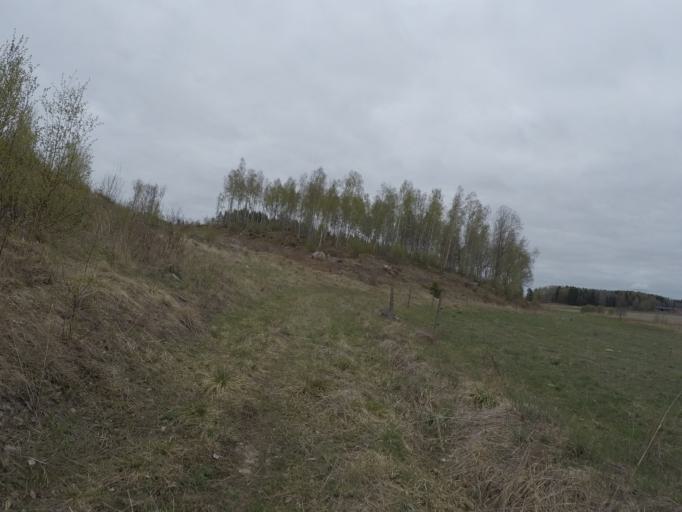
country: SE
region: Soedermanland
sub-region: Eskilstuna Kommun
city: Kvicksund
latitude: 59.4241
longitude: 16.2684
